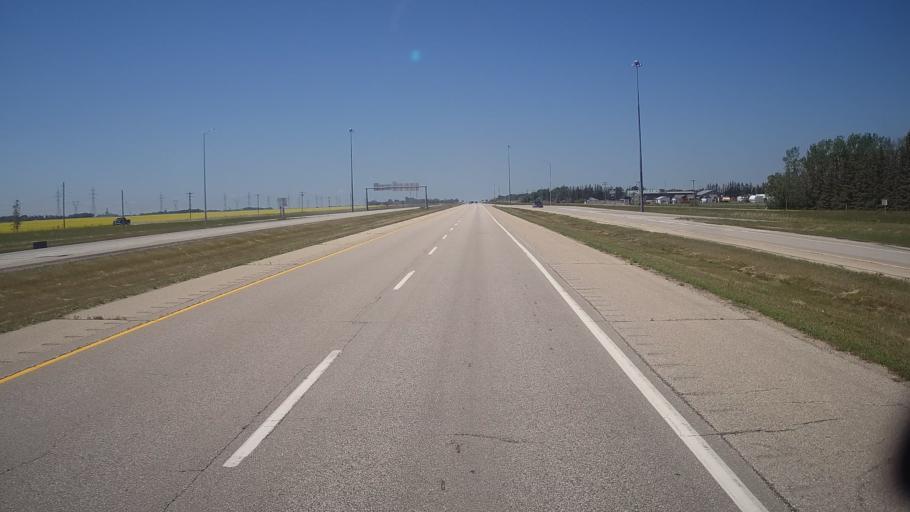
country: CA
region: Manitoba
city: Winnipeg
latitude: 49.9900
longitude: -97.2336
